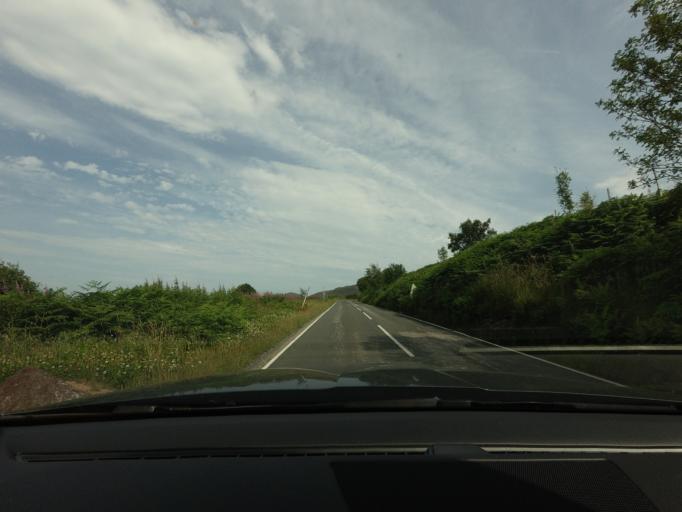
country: GB
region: Scotland
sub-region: Highland
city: Alness
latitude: 57.8433
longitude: -4.2889
